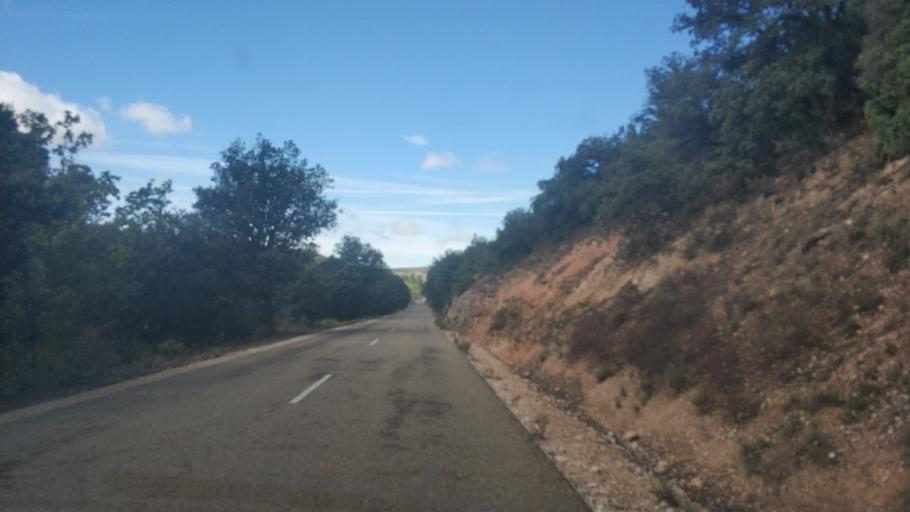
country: ES
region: Castille and Leon
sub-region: Provincia de Burgos
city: Covarrubias
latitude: 42.0524
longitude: -3.4988
